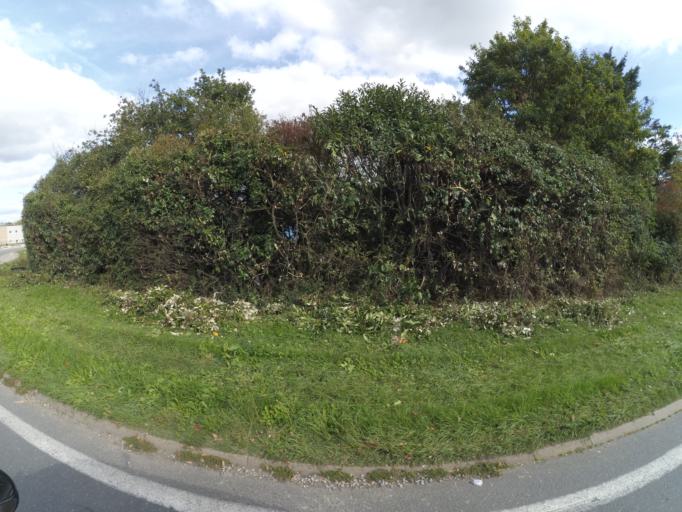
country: FR
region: Pays de la Loire
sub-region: Departement de la Loire-Atlantique
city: Thouare-sur-Loire
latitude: 47.2821
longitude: -1.4533
